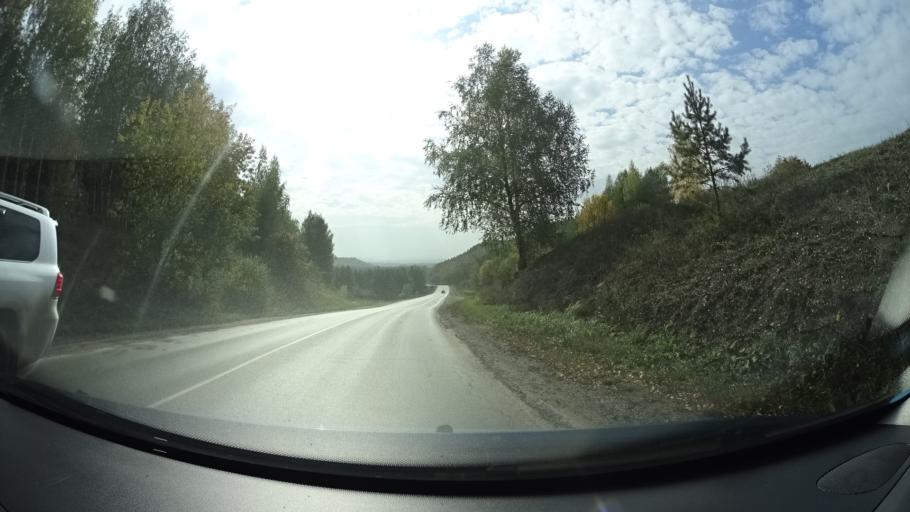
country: RU
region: Bashkortostan
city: Oktyabr'skiy
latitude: 54.5397
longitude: 53.5646
